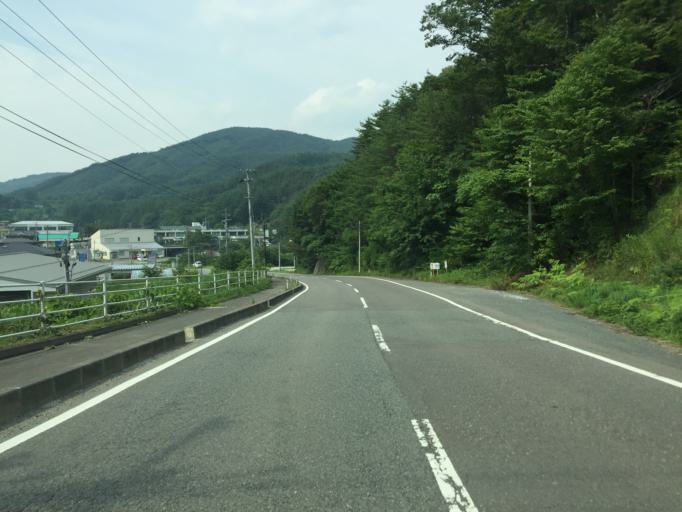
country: JP
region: Fukushima
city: Funehikimachi-funehiki
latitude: 37.4997
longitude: 140.7645
